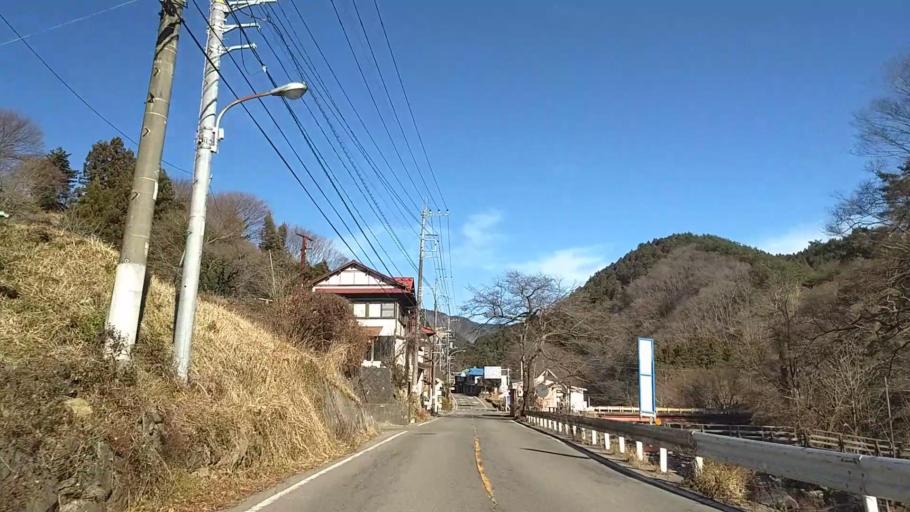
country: JP
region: Yamanashi
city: Otsuki
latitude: 35.5216
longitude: 139.0220
